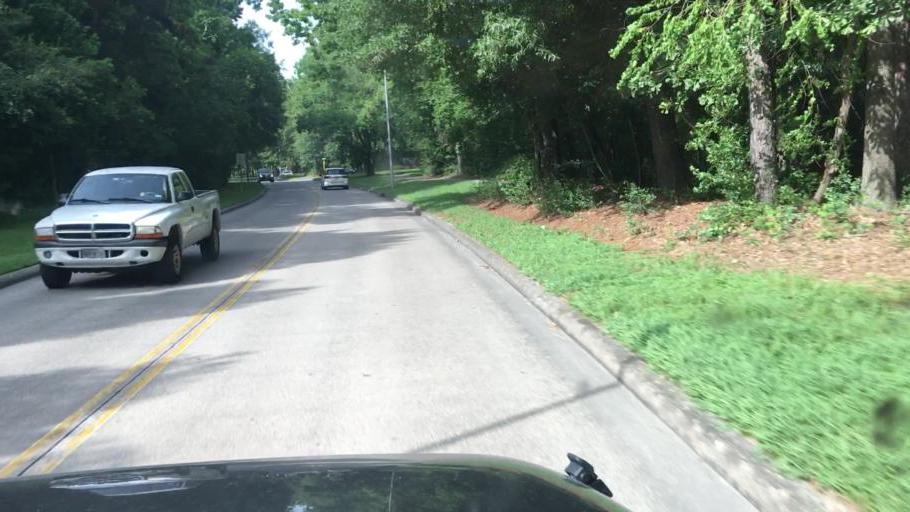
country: US
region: Texas
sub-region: Harris County
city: Atascocita
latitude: 30.0054
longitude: -95.1741
